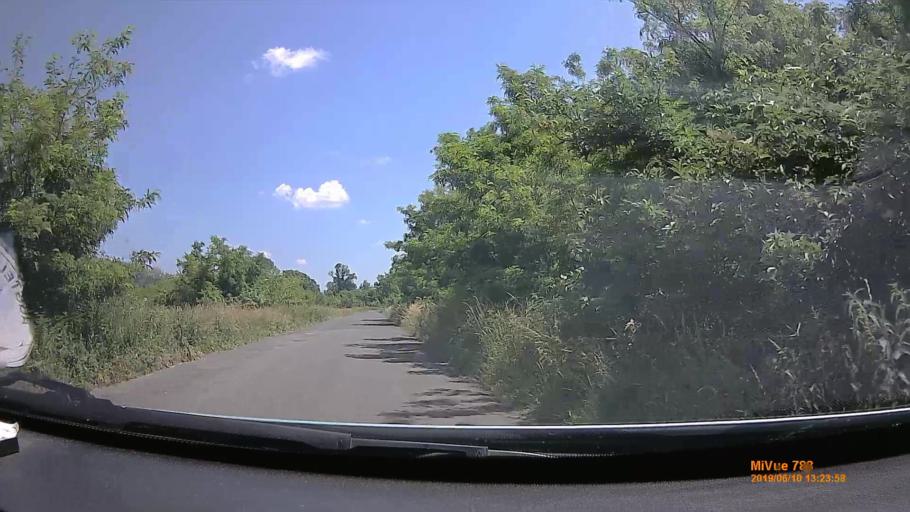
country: HU
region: Borsod-Abauj-Zemplen
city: Tiszaluc
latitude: 48.0235
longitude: 21.0982
